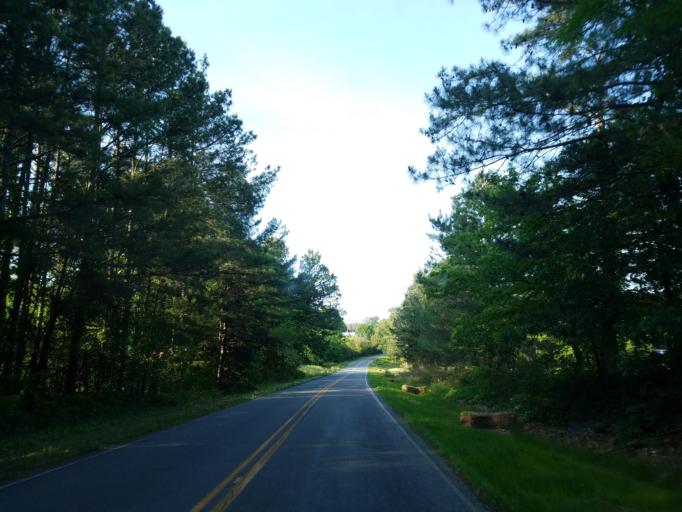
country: US
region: Georgia
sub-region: Floyd County
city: Shannon
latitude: 34.4853
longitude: -85.1341
